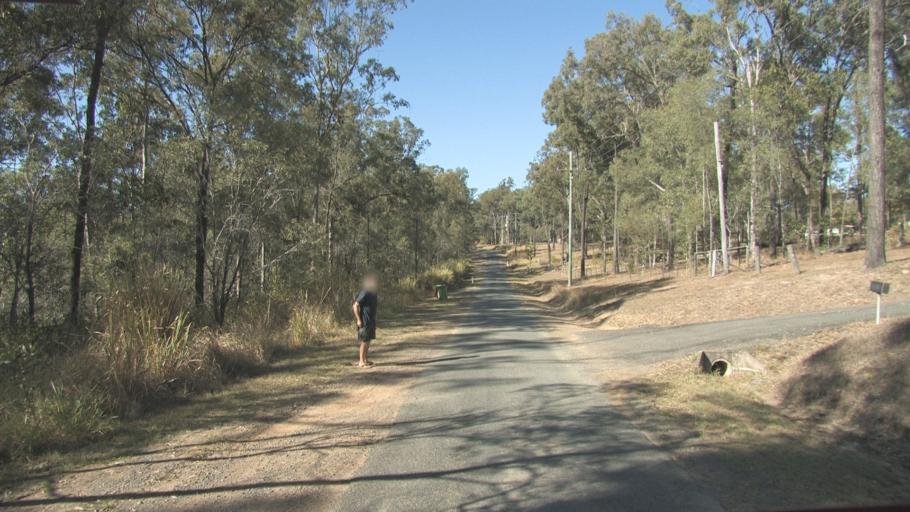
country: AU
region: Queensland
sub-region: Logan
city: Cedar Vale
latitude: -27.8416
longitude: 153.0684
